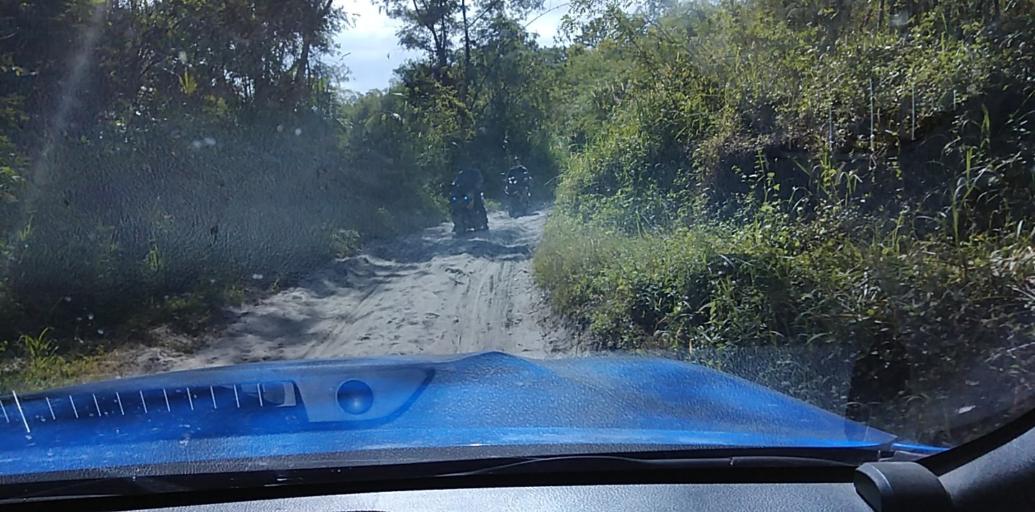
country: PH
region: Central Luzon
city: Santol
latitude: 15.1714
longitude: 120.4790
